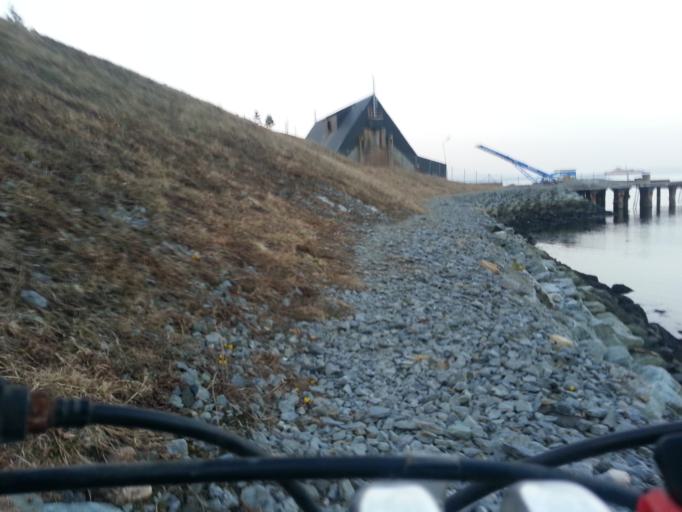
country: NO
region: Sor-Trondelag
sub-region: Trondheim
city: Trondheim
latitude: 63.4360
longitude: 10.3504
